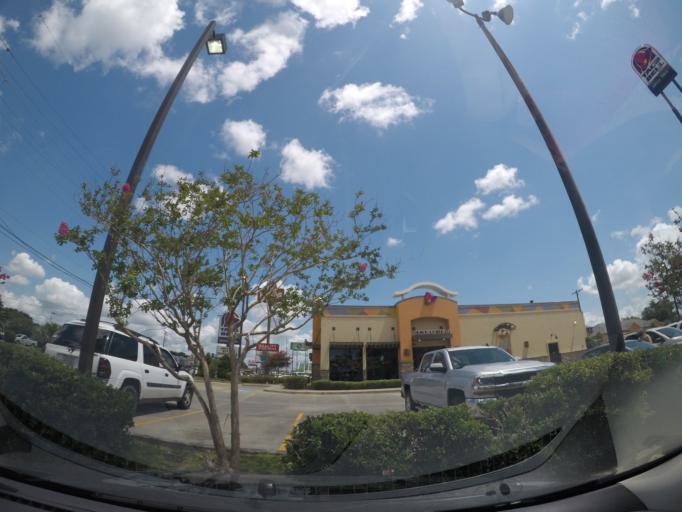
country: US
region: Louisiana
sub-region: Calcasieu Parish
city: Sulphur
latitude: 30.2190
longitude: -93.3759
